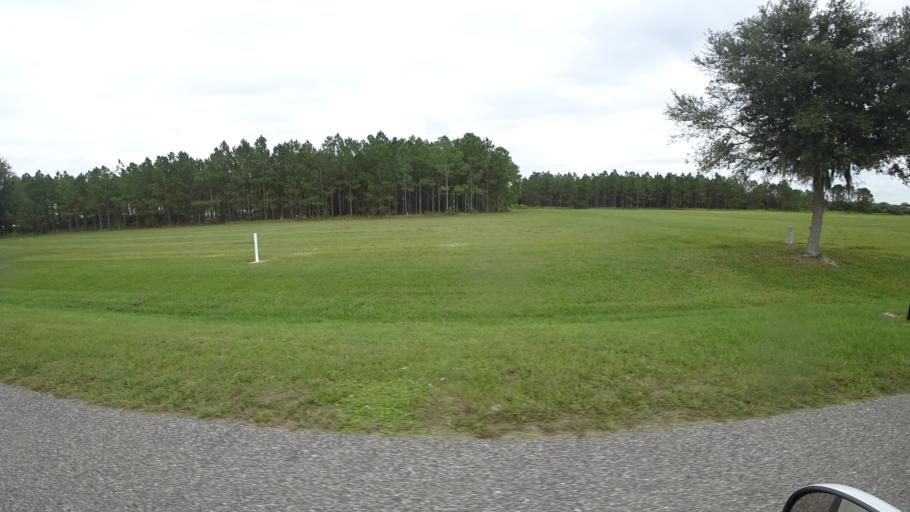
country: US
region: Florida
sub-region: Hillsborough County
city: Wimauma
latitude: 27.6559
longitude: -82.3256
